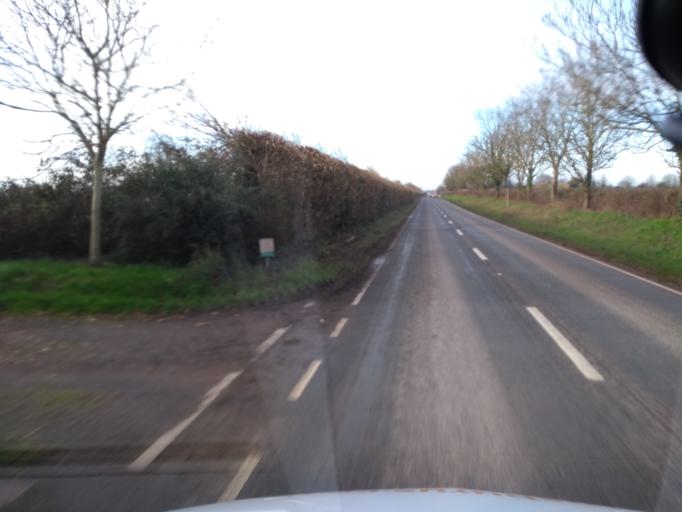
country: GB
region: England
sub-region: Somerset
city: Westonzoyland
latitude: 51.0523
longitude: -2.9620
